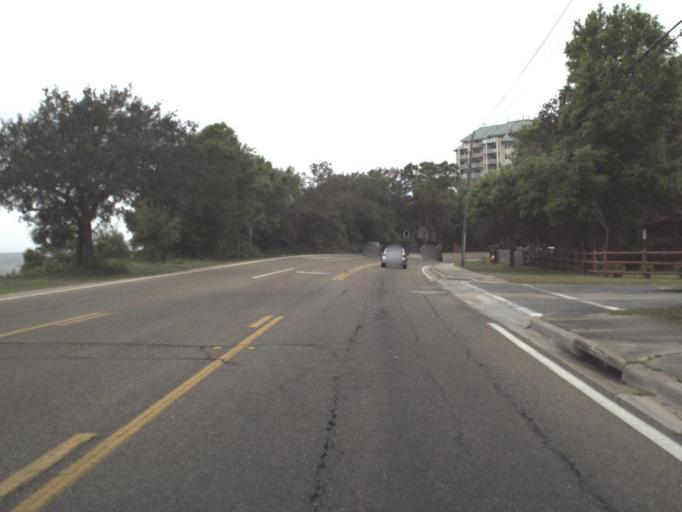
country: US
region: Florida
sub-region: Escambia County
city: East Pensacola Heights
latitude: 30.4369
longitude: -87.1738
